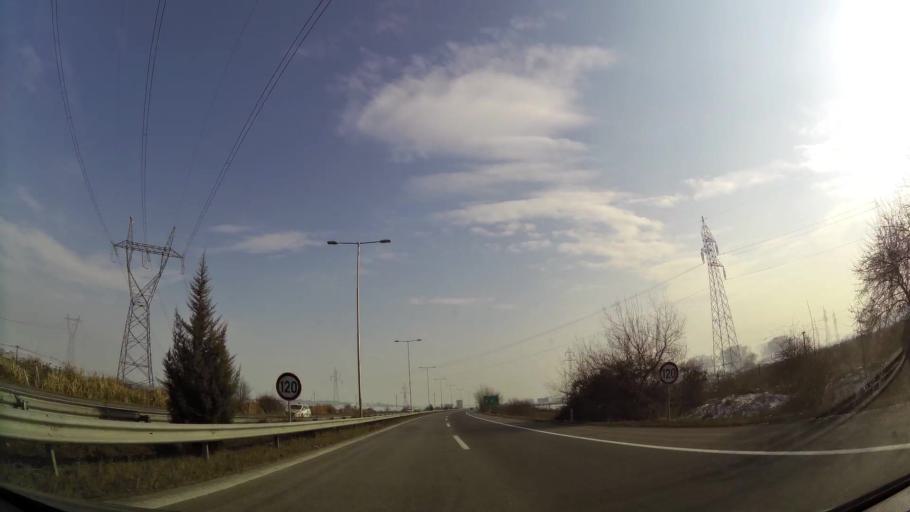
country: MK
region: Butel
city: Butel
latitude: 42.0393
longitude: 21.4623
